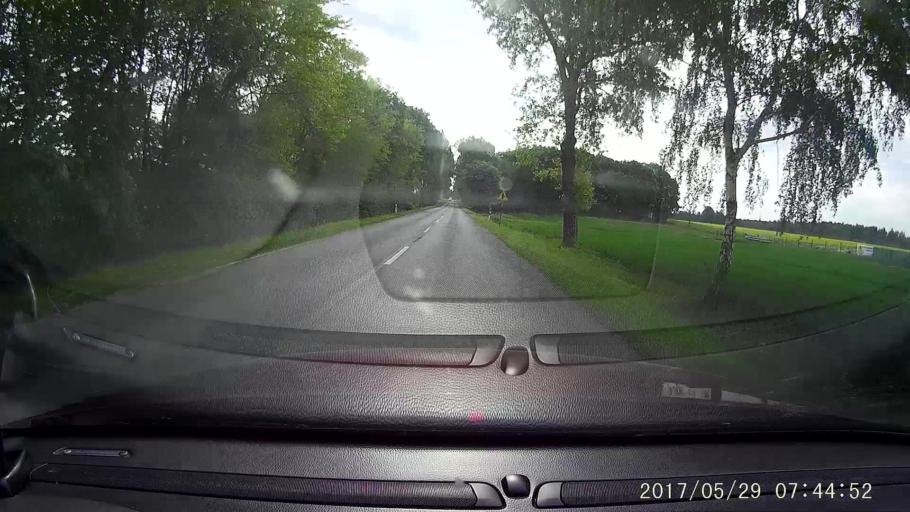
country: PL
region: Lower Silesian Voivodeship
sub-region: Powiat boleslawiecki
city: Boleslawiec
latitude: 51.2390
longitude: 15.6133
